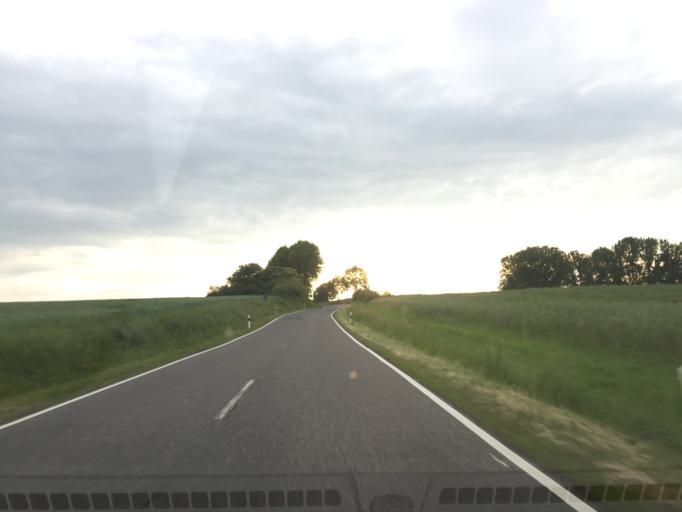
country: DE
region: Rheinland-Pfalz
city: Hundsangen
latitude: 50.4536
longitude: 8.0123
